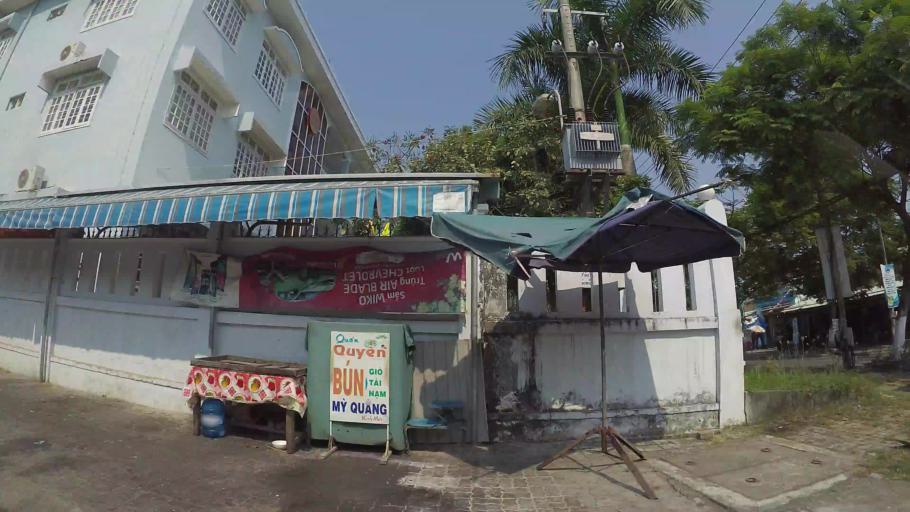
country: VN
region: Da Nang
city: Cam Le
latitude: 16.0116
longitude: 108.1972
